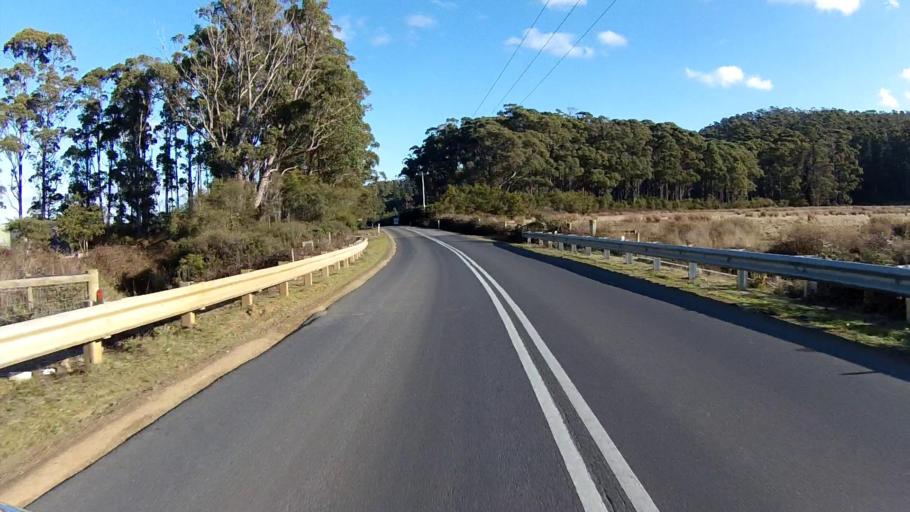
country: AU
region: Tasmania
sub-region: Clarence
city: Sandford
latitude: -43.1067
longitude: 147.8630
